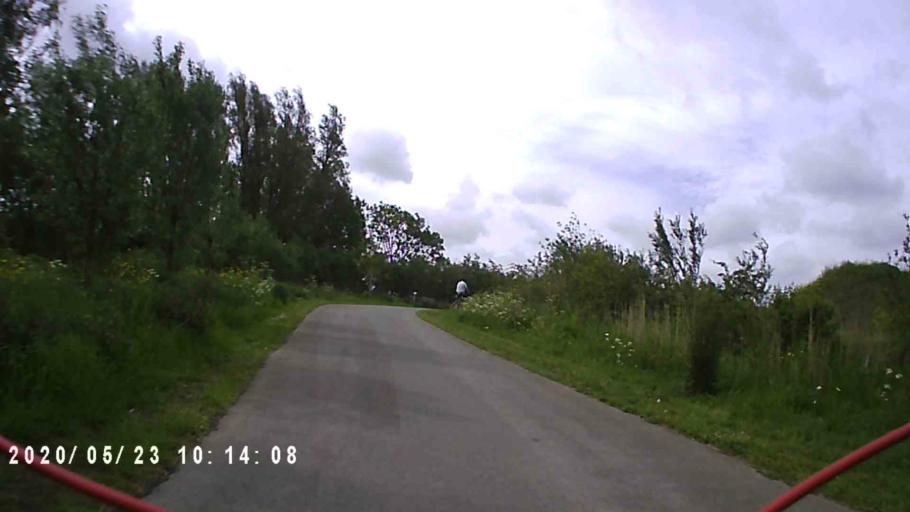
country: NL
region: Groningen
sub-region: Gemeente Appingedam
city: Appingedam
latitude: 53.3129
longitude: 6.8549
